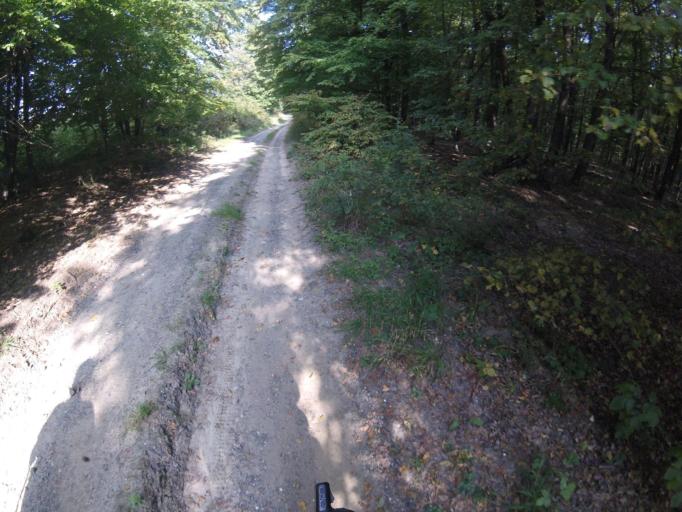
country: HU
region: Komarom-Esztergom
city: Kesztolc
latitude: 47.7649
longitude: 18.8141
